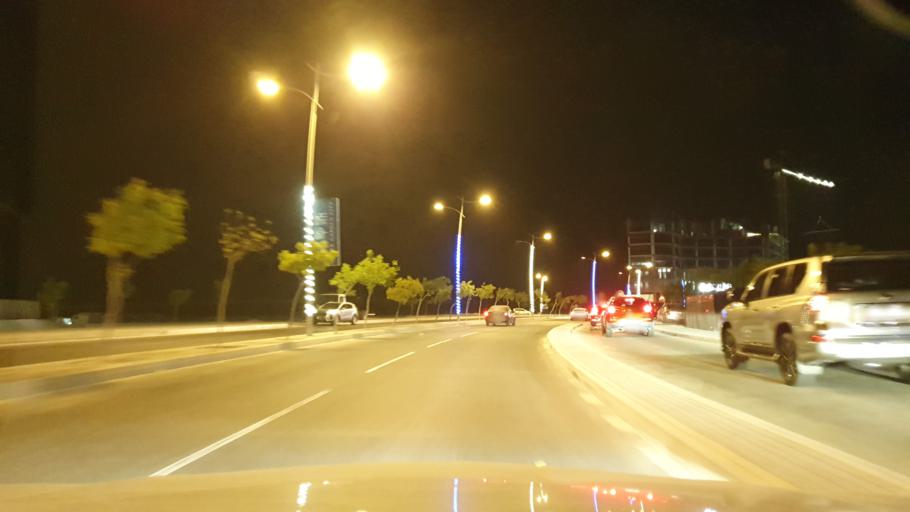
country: BH
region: Manama
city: Jidd Hafs
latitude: 26.2419
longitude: 50.5524
